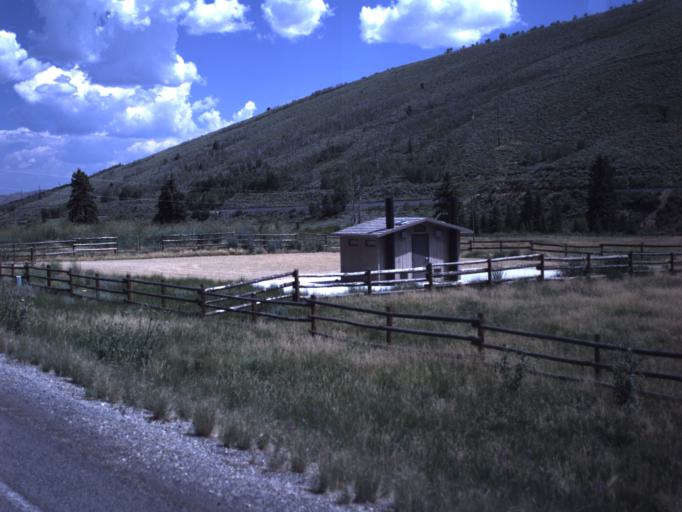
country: US
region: Utah
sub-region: Sanpete County
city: Fairview
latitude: 39.7078
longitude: -111.1632
